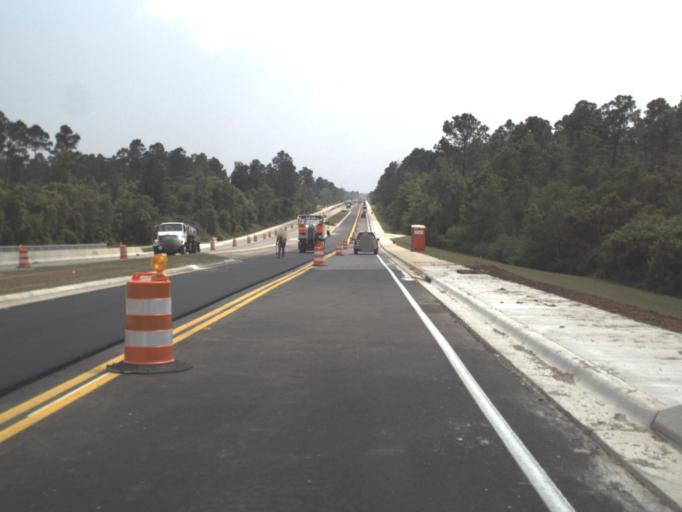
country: US
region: Florida
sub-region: Santa Rosa County
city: Bagdad
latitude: 30.5676
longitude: -87.0872
